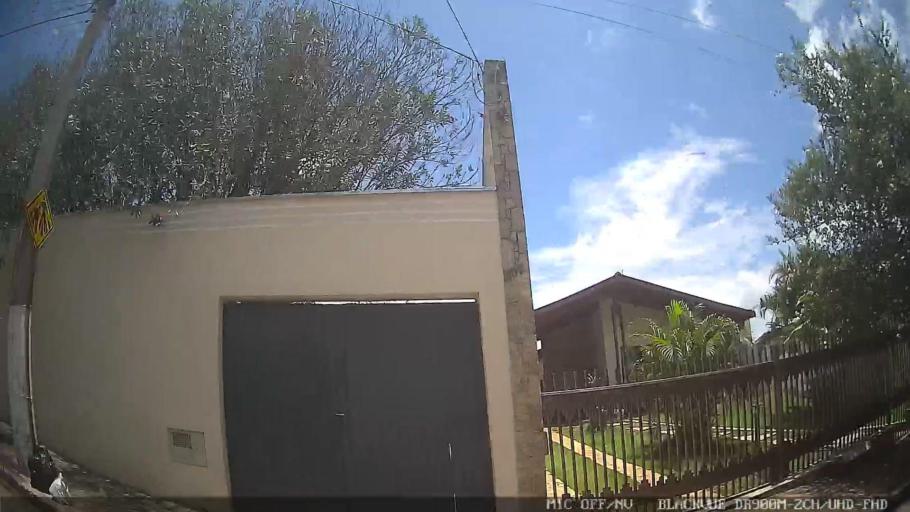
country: BR
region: Sao Paulo
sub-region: Laranjal Paulista
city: Laranjal Paulista
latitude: -23.0495
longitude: -47.8344
